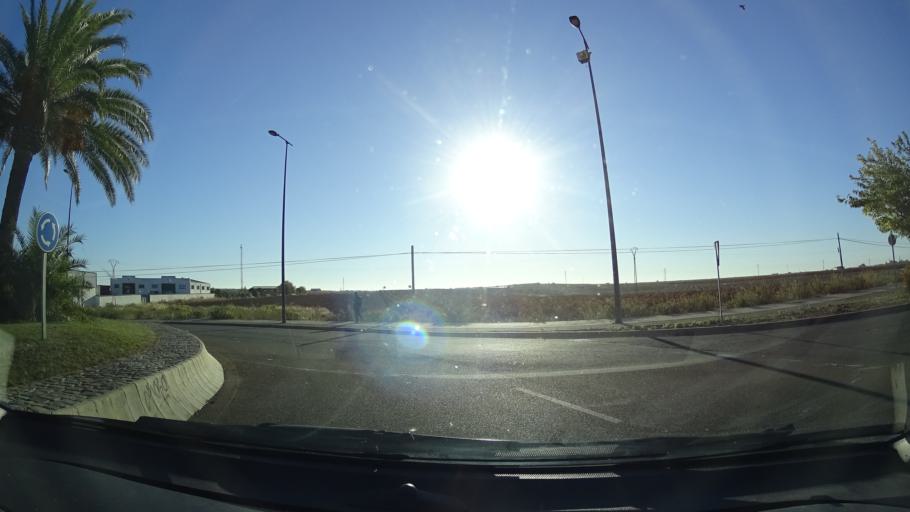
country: ES
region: Extremadura
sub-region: Provincia de Badajoz
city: Almendralejo
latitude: 38.7043
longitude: -6.4014
